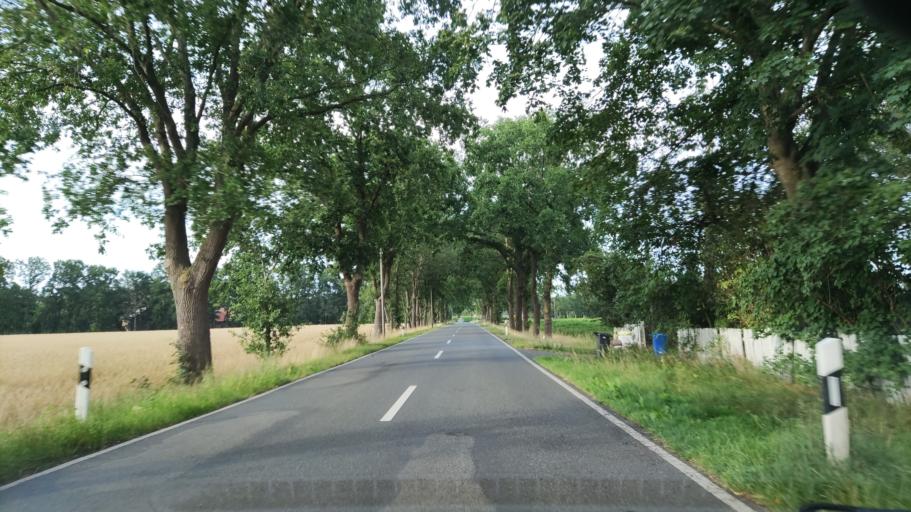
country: DE
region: Lower Saxony
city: Jameln
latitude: 53.0520
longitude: 11.1357
